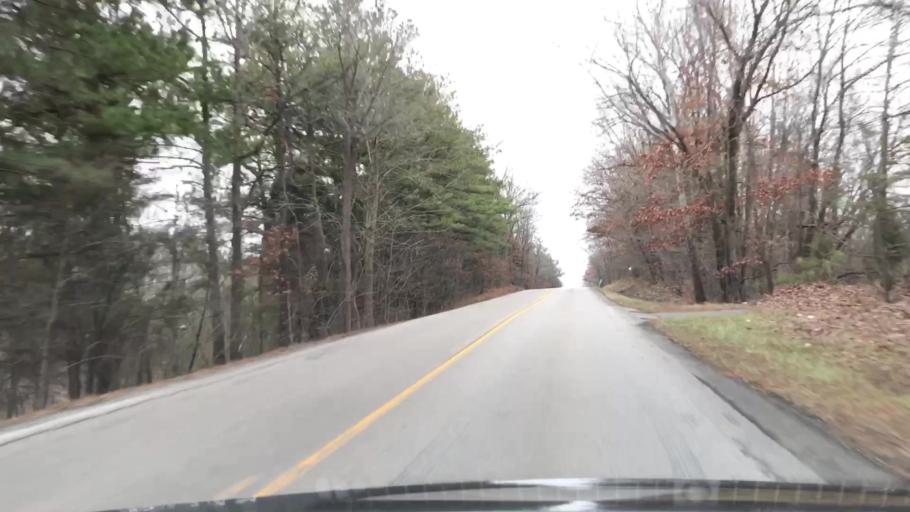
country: US
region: Kentucky
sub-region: Muhlenberg County
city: Morehead
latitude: 37.2874
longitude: -87.2105
